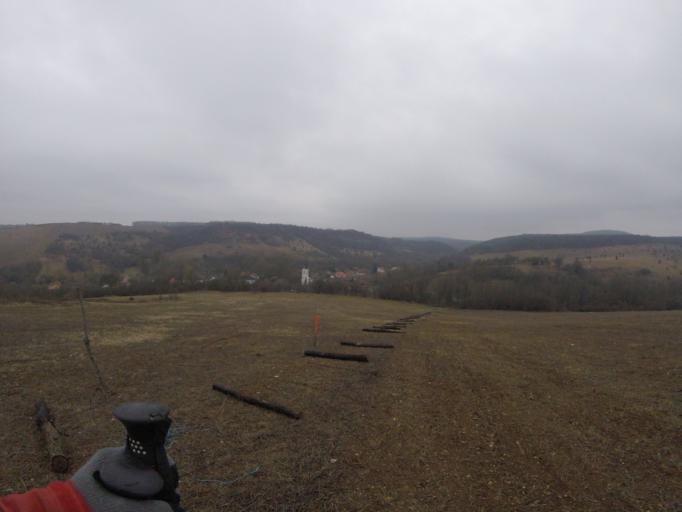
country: HU
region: Borsod-Abauj-Zemplen
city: Rudabanya
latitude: 48.4447
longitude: 20.5911
